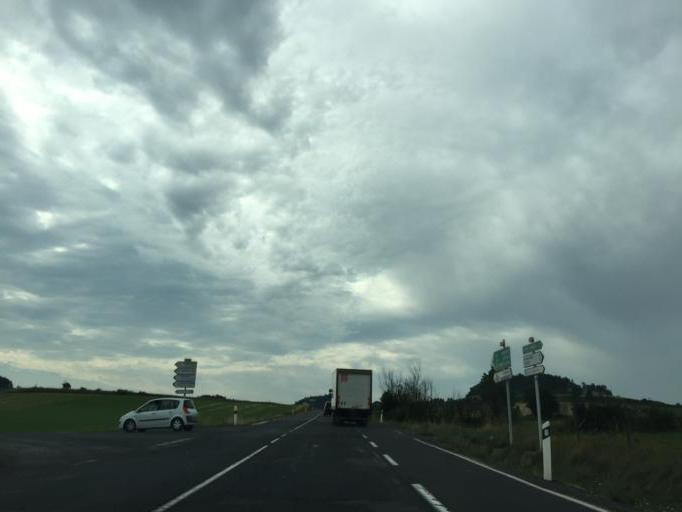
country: FR
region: Auvergne
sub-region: Departement de la Haute-Loire
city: Solignac-sur-Loire
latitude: 44.9559
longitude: 3.8435
